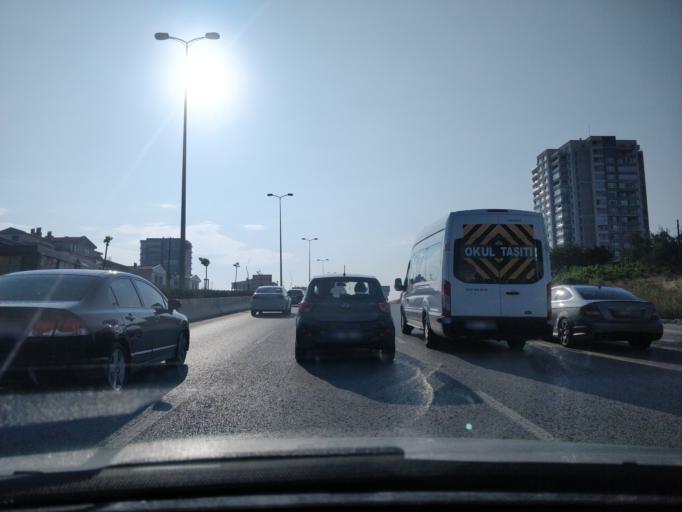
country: TR
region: Ankara
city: Etimesgut
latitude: 39.8977
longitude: 32.6491
